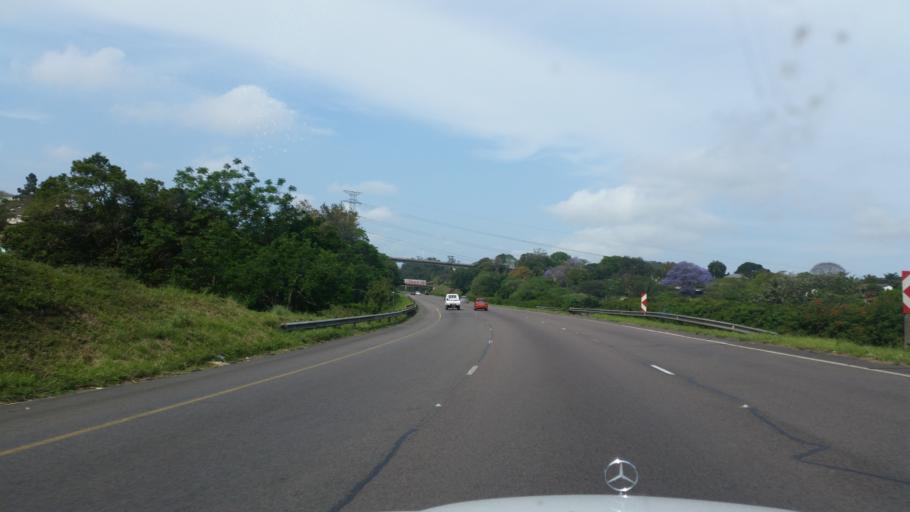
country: ZA
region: KwaZulu-Natal
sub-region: eThekwini Metropolitan Municipality
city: Berea
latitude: -29.8384
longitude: 30.8708
